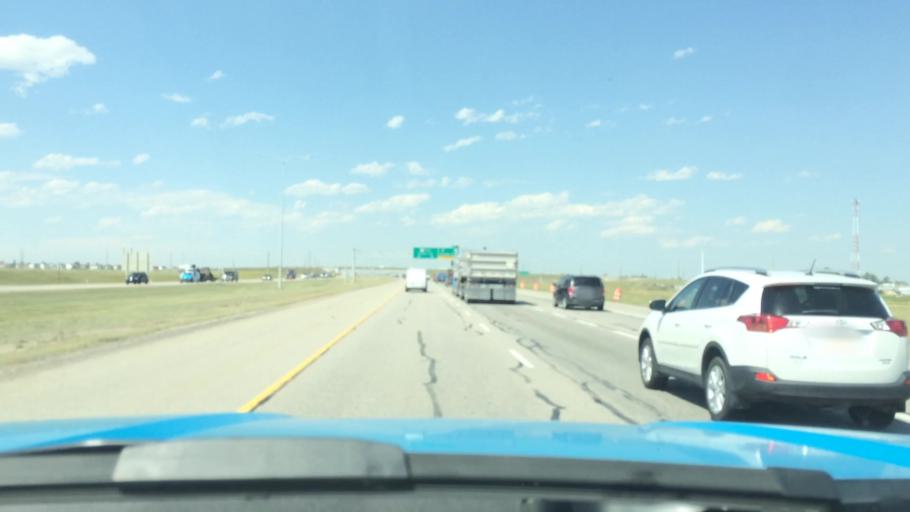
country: CA
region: Alberta
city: Chestermere
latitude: 51.0876
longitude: -113.9191
